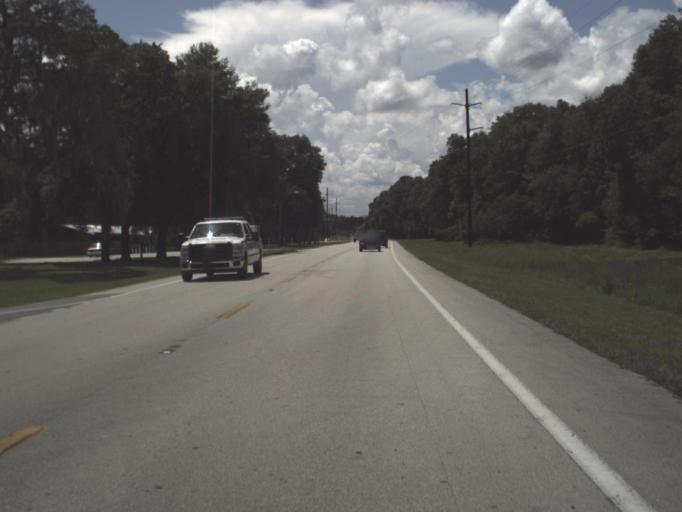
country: US
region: Florida
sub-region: Putnam County
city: Crescent City
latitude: 29.5032
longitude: -81.6020
